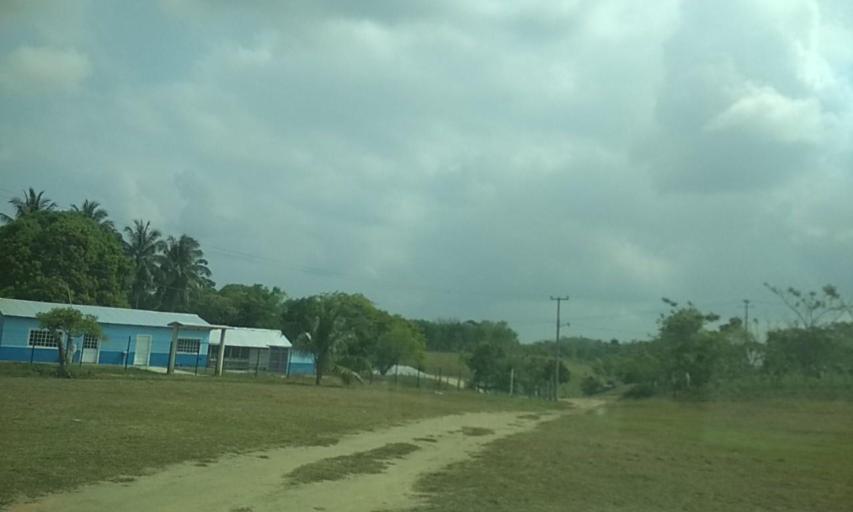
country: MX
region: Tabasco
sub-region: Huimanguillo
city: Francisco Rueda
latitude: 17.6544
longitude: -93.7547
